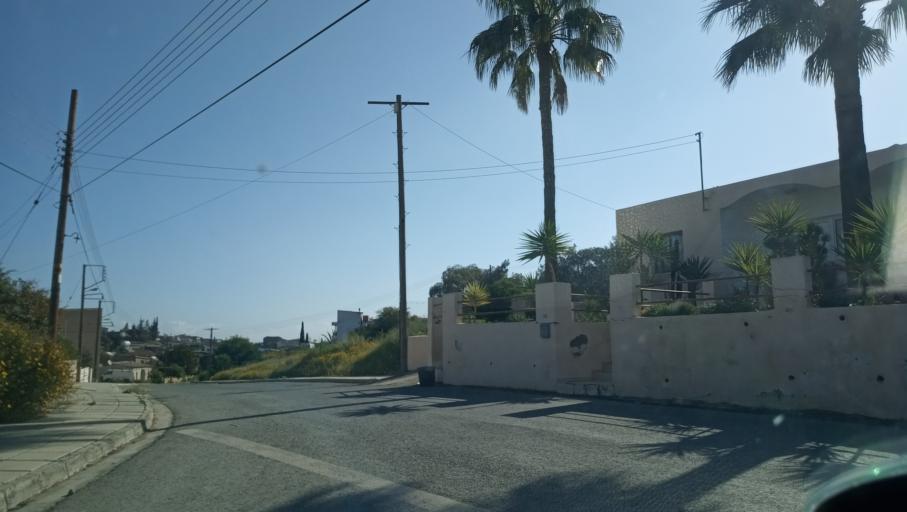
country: CY
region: Lefkosia
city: Tseri
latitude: 35.0708
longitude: 33.3190
